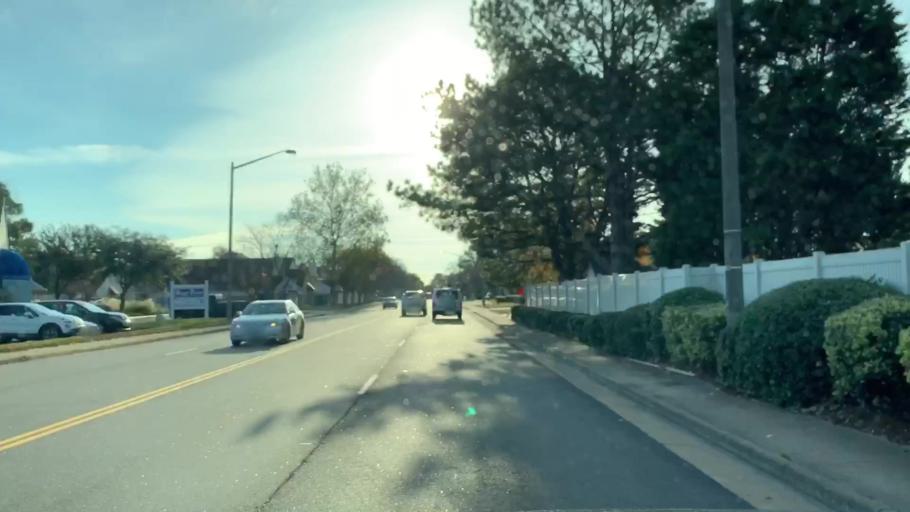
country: US
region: Virginia
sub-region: City of Chesapeake
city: Chesapeake
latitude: 36.7923
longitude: -76.1682
